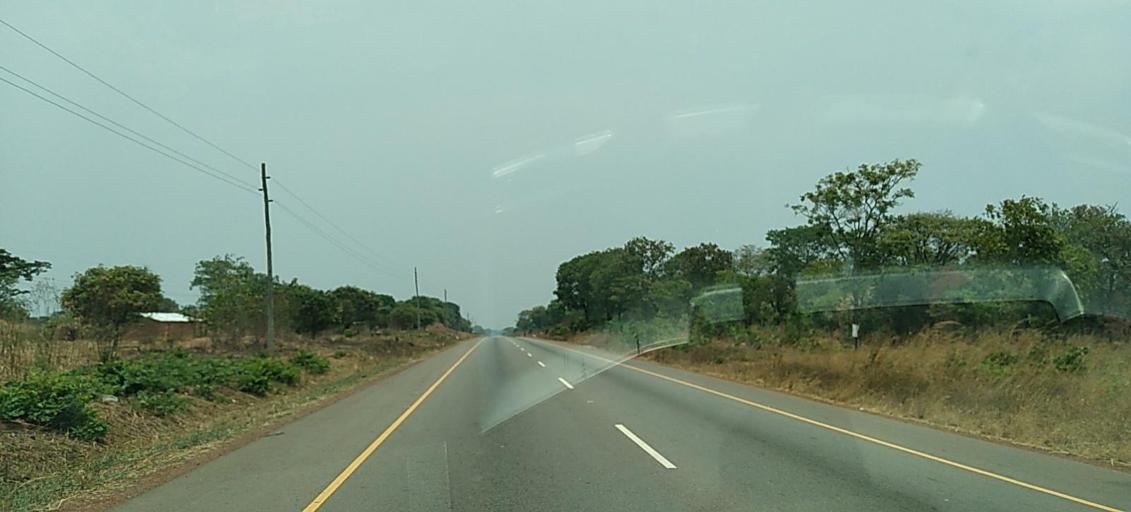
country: ZM
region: Copperbelt
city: Chililabombwe
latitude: -12.4996
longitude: 27.5383
